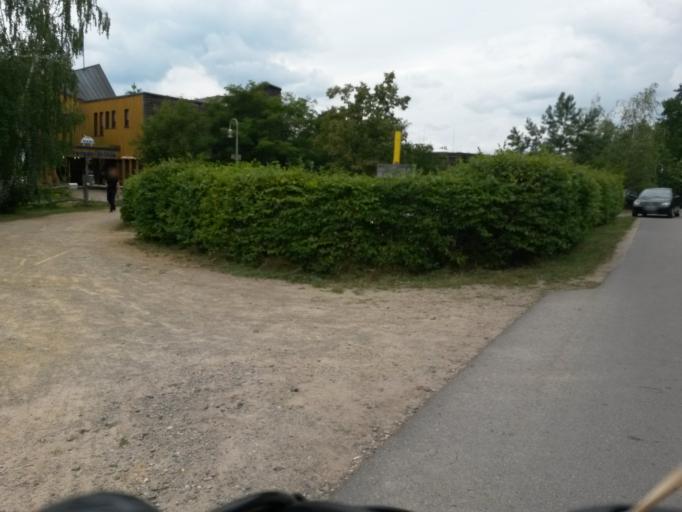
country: DE
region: Brandenburg
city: Angermunde
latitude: 53.0351
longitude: 13.9665
